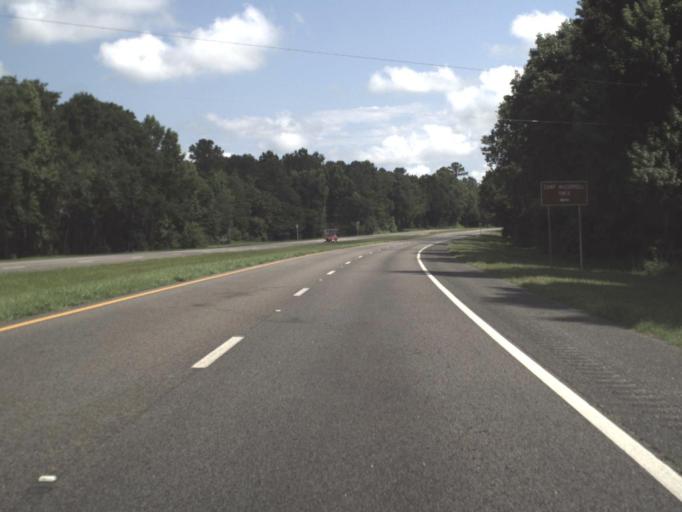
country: US
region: Florida
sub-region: Alachua County
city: Gainesville
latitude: 29.5278
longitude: -82.3079
